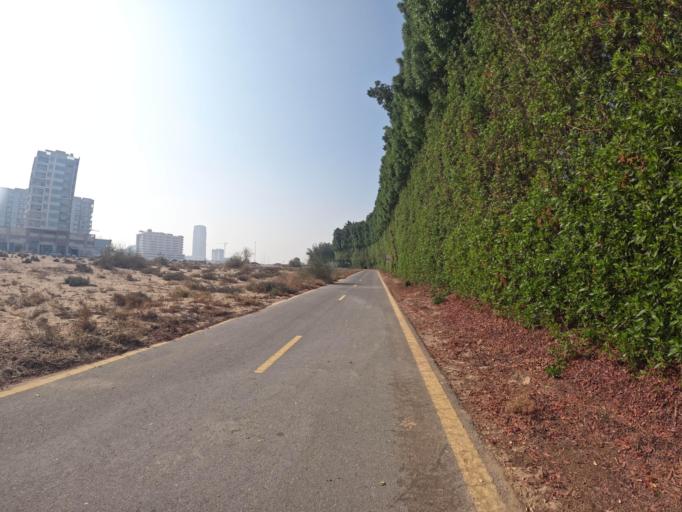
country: AE
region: Dubai
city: Dubai
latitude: 25.0973
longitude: 55.3136
